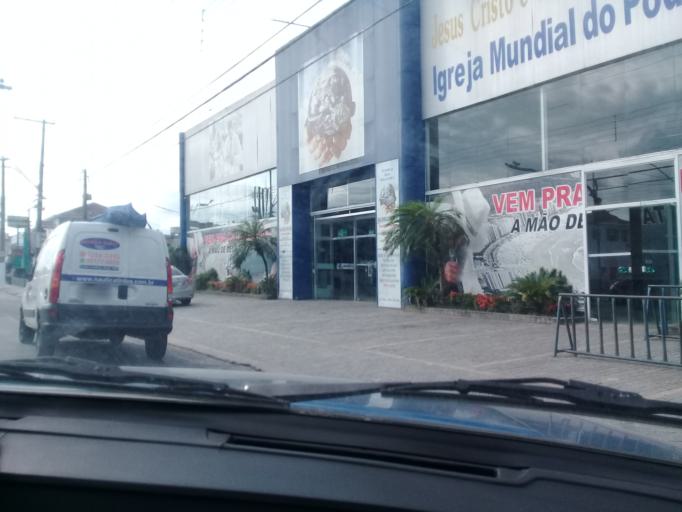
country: BR
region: Sao Paulo
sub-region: Guaruja
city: Guaruja
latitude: -23.9909
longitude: -46.2809
